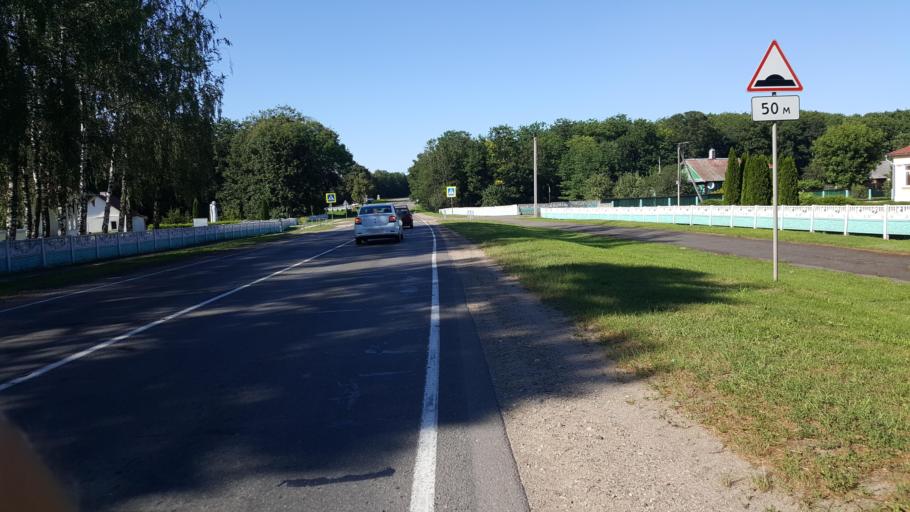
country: BY
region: Brest
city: Charnawchytsy
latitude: 52.2708
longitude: 23.7689
